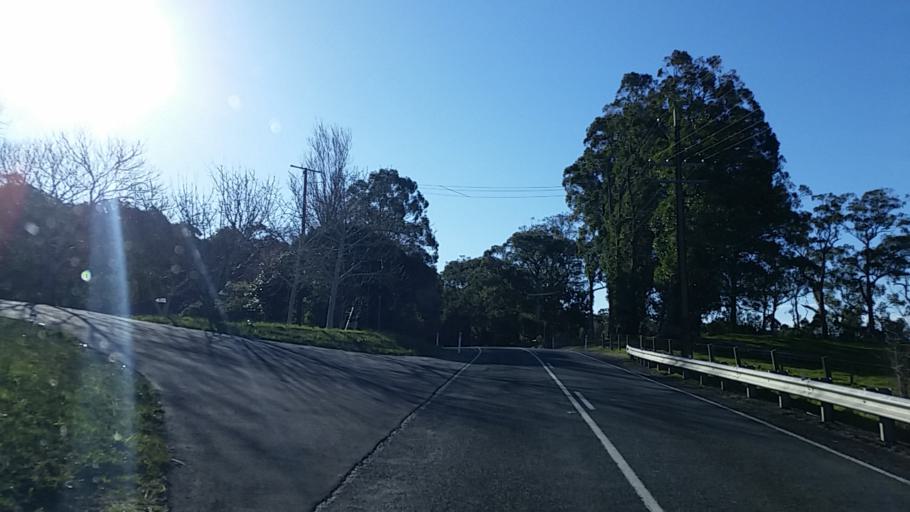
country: AU
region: South Australia
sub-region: Adelaide Hills
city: Crafers
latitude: -34.9572
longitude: 138.7193
